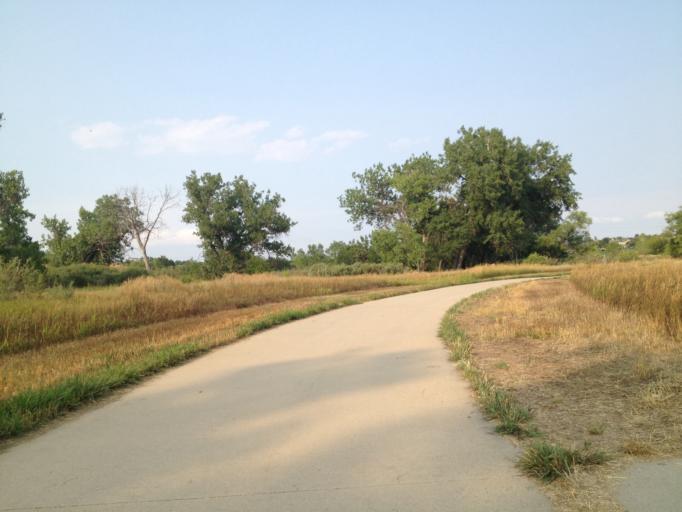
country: US
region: Colorado
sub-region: Broomfield County
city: Broomfield
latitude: 39.8893
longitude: -105.0640
